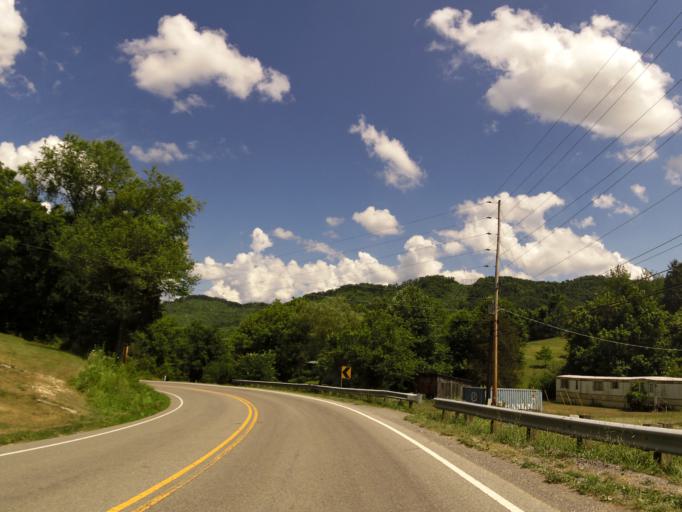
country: US
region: Virginia
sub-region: Lee County
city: Pennington Gap
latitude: 36.6933
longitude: -83.0247
